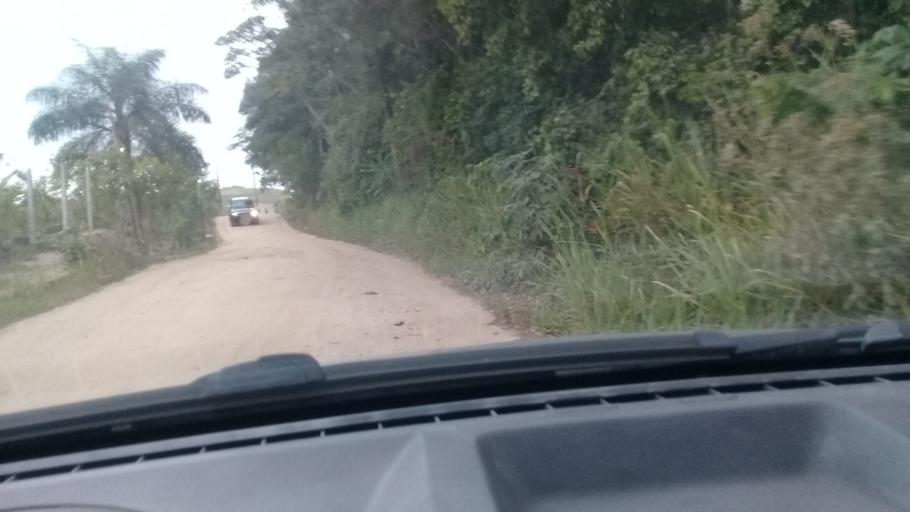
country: BR
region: Pernambuco
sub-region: Jaboatao Dos Guararapes
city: Jaboatao dos Guararapes
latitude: -8.0828
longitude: -35.0342
